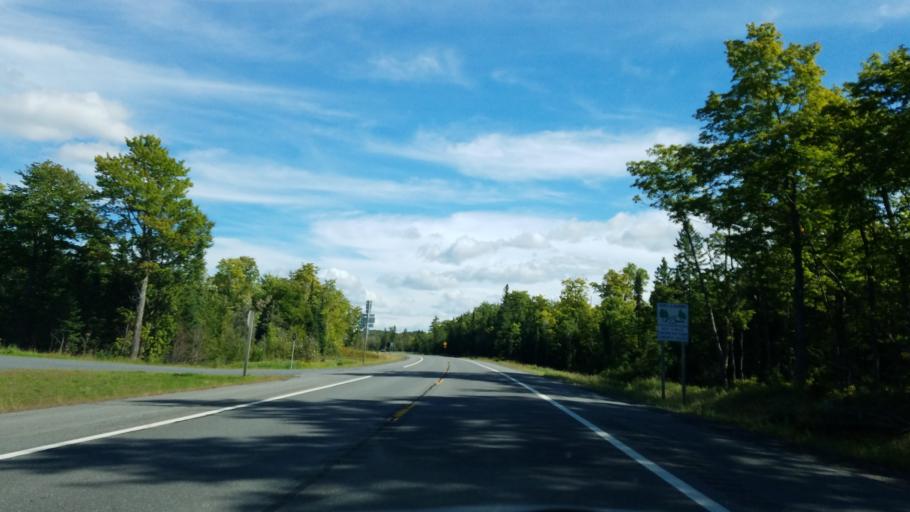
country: US
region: Michigan
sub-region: Baraga County
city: L'Anse
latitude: 46.5839
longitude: -88.4704
